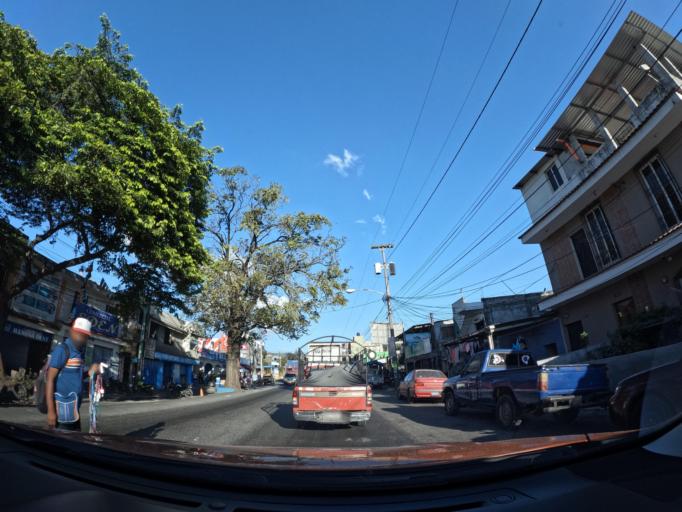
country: GT
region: Escuintla
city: Palin
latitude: 14.4037
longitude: -90.6957
